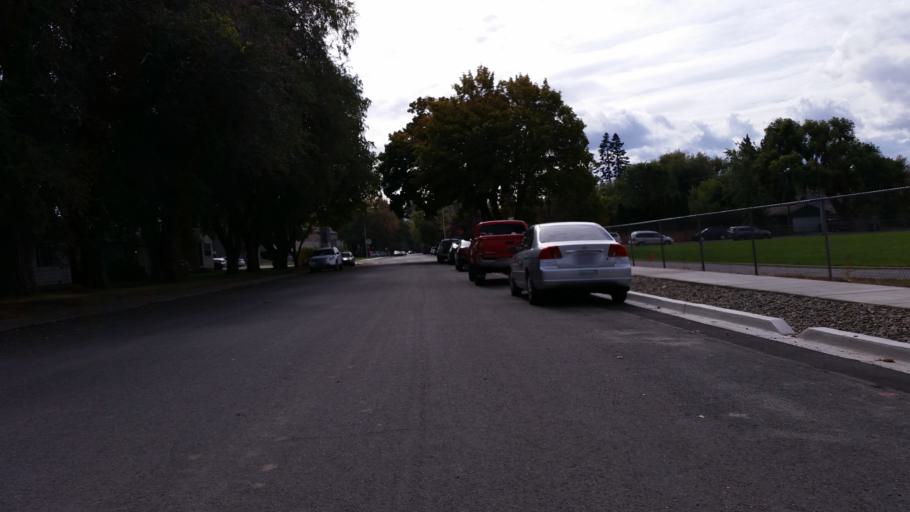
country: US
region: Washington
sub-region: Kittitas County
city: Ellensburg
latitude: 46.9923
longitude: -120.5404
